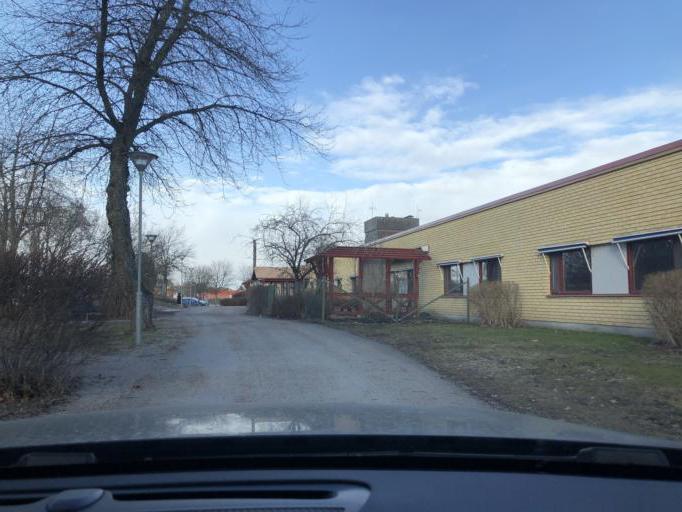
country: SE
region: Uppsala
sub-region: Tierps Kommun
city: Tierp
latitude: 60.3366
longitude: 17.5127
